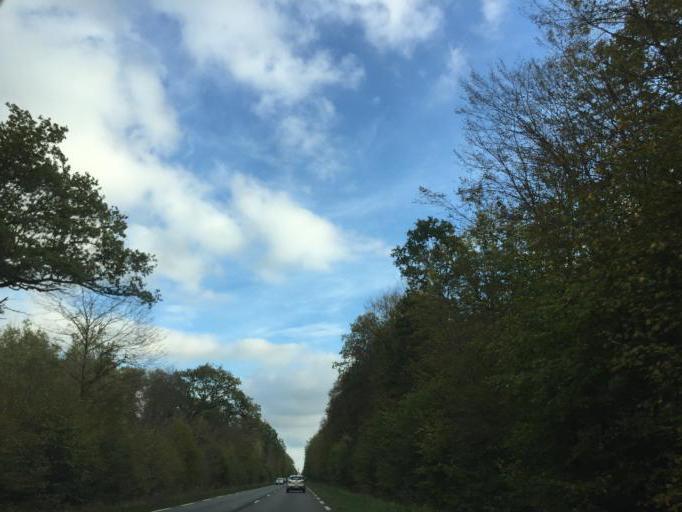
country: FR
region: Ile-de-France
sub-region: Departement de Seine-et-Marne
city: Villeneuve-le-Comte
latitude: 48.7970
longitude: 2.8588
